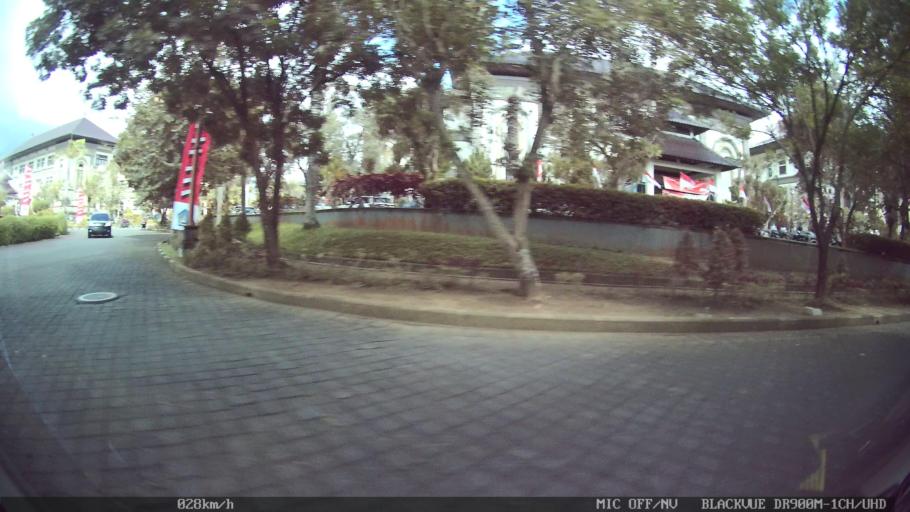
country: ID
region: Bali
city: Banjar Karangsuling
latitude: -8.6046
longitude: 115.1799
